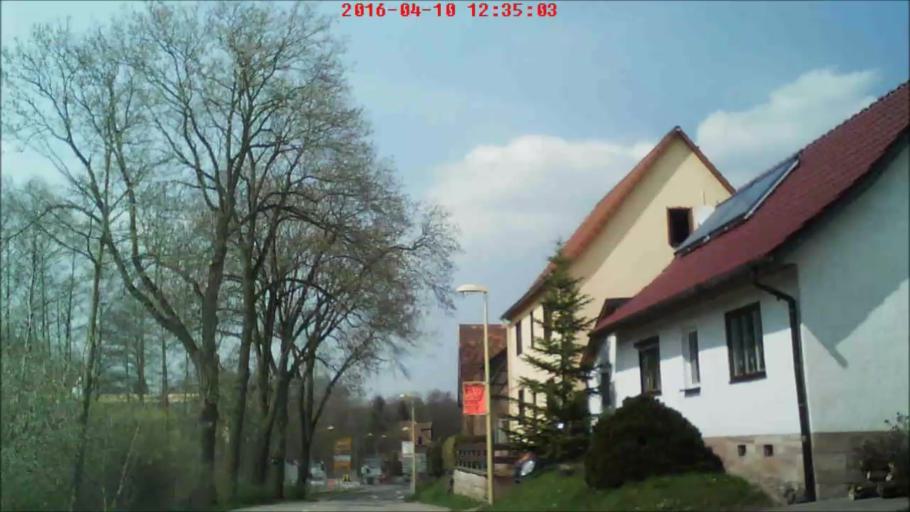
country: DE
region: Thuringia
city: Schmalkalden
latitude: 50.7147
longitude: 10.4716
